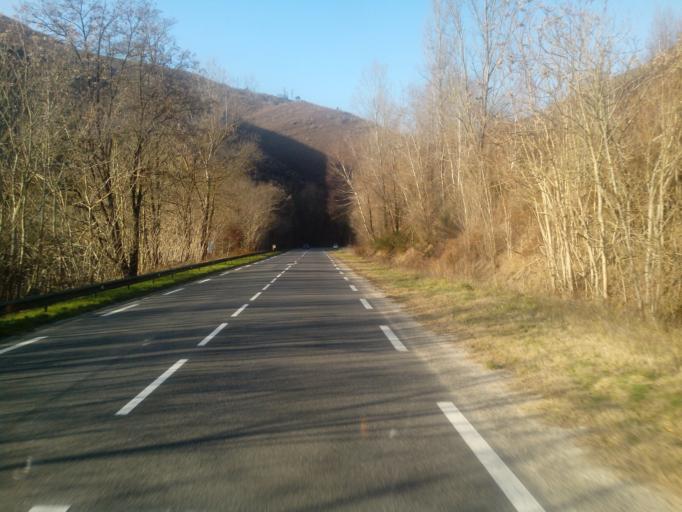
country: FR
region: Midi-Pyrenees
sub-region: Departement de l'Aveyron
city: Viviez
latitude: 44.5679
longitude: 2.2102
